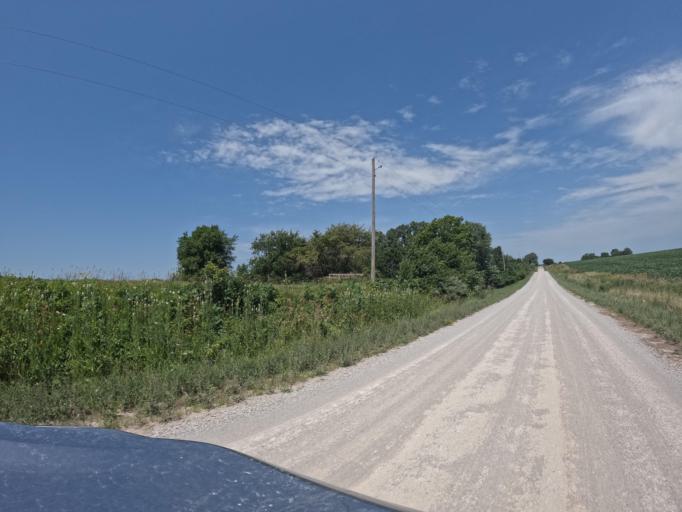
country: US
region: Iowa
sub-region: Appanoose County
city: Centerville
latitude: 40.7894
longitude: -92.9160
